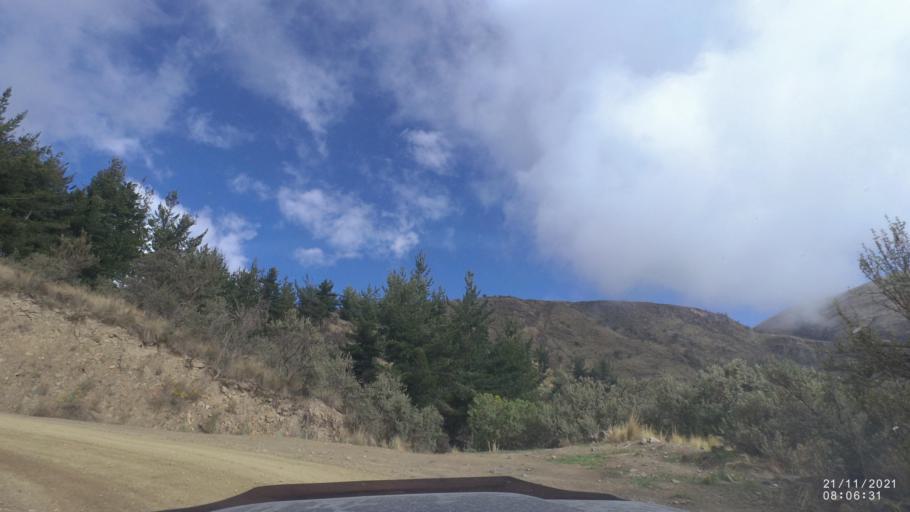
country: BO
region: Cochabamba
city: Cochabamba
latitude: -17.2877
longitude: -66.2097
